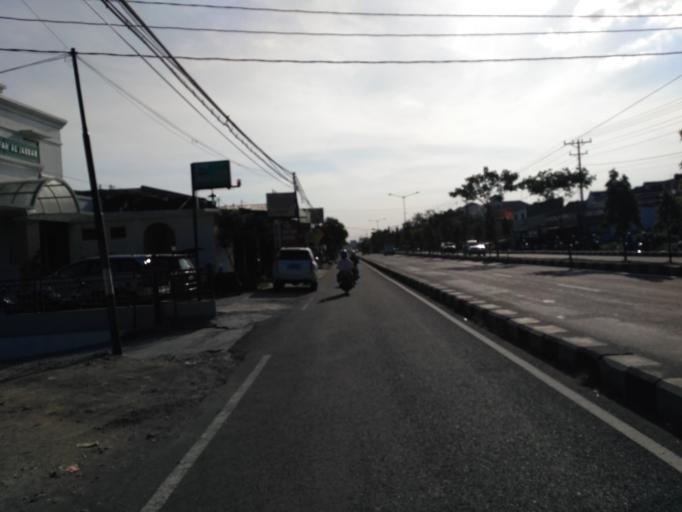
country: ID
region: Daerah Istimewa Yogyakarta
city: Depok
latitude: -7.7646
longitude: 110.4230
